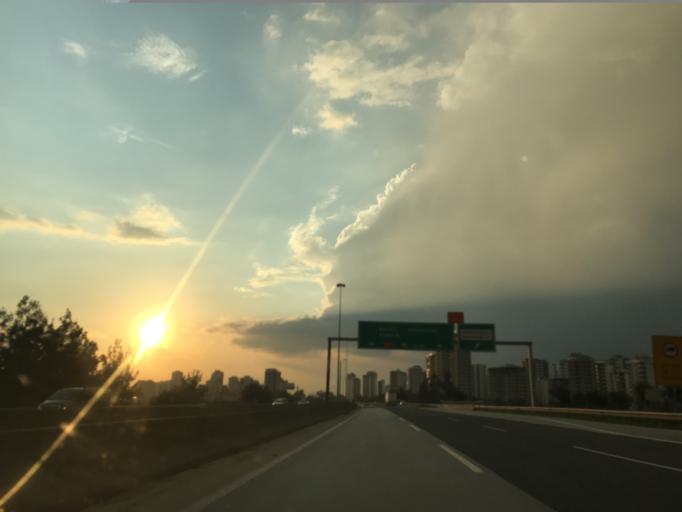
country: TR
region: Adana
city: Seyhan
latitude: 37.0326
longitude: 35.2551
